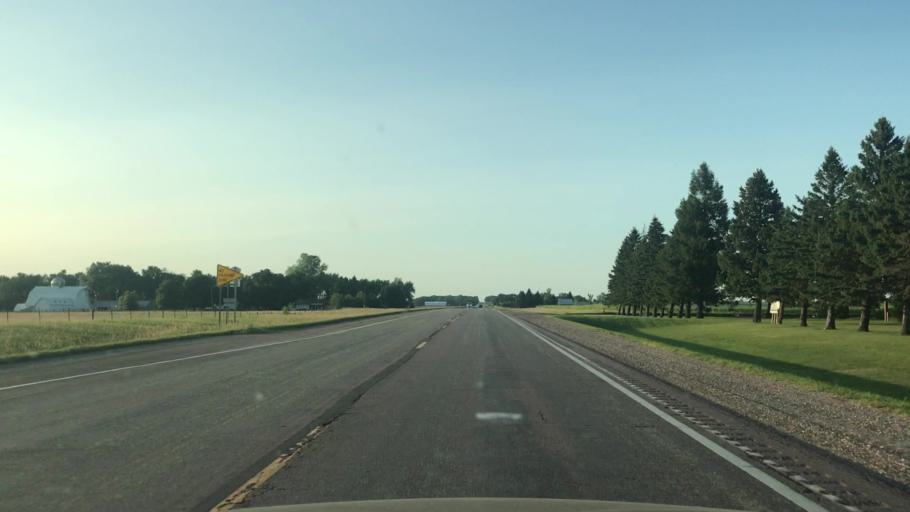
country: US
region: Minnesota
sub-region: Cottonwood County
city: Windom
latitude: 43.9068
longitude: -95.1203
